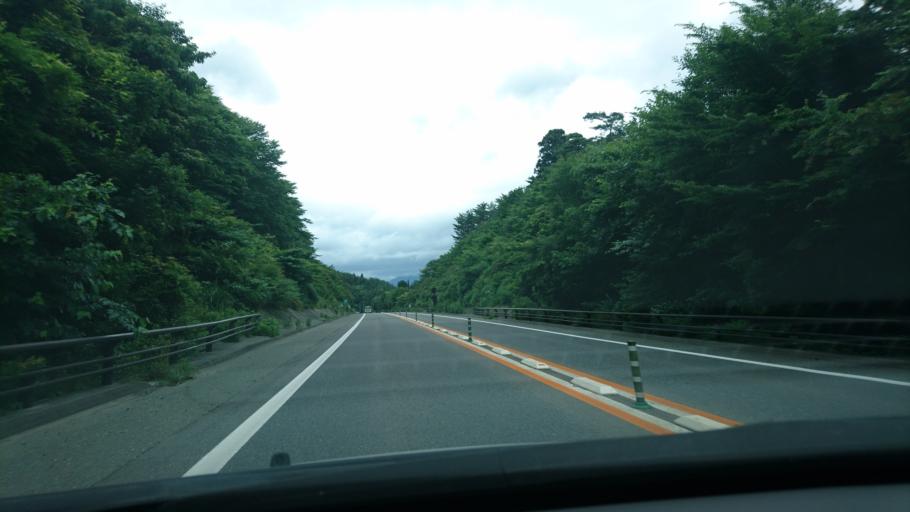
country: JP
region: Iwate
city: Ofunato
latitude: 39.0505
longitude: 141.7145
